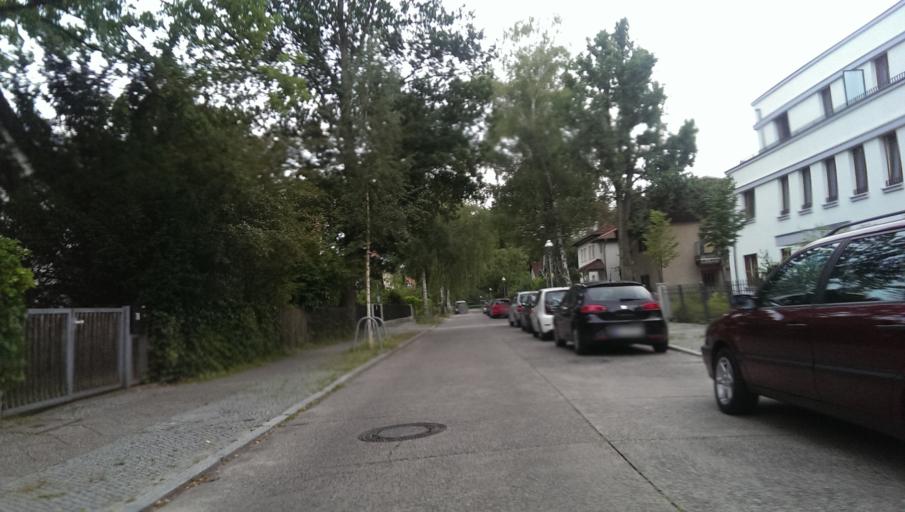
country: DE
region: Brandenburg
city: Teltow
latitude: 52.4188
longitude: 13.2630
